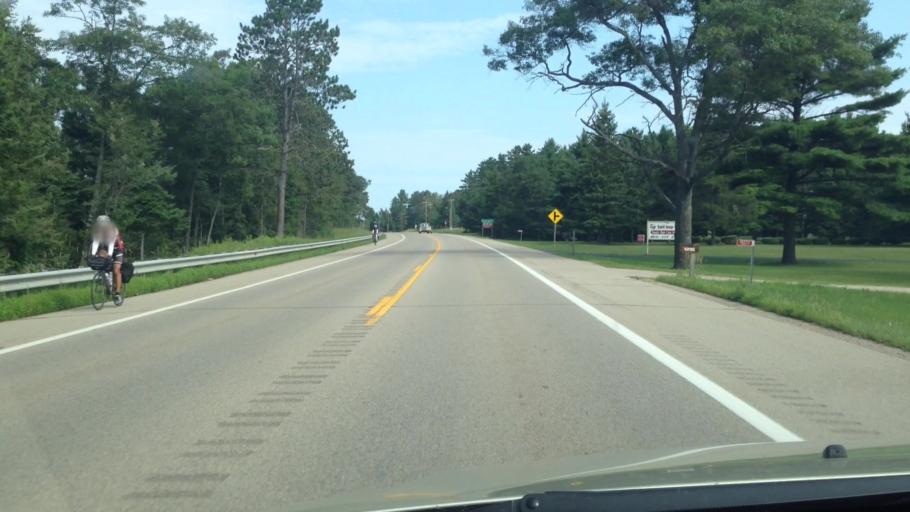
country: US
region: Michigan
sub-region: Delta County
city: Gladstone
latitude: 45.9181
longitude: -86.9334
